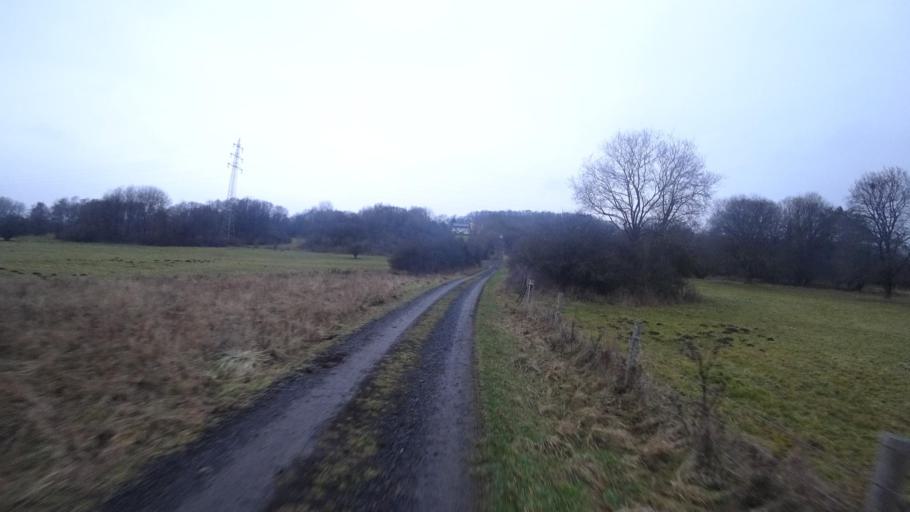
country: DE
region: Rheinland-Pfalz
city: Bellingen
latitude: 50.6001
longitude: 7.9105
